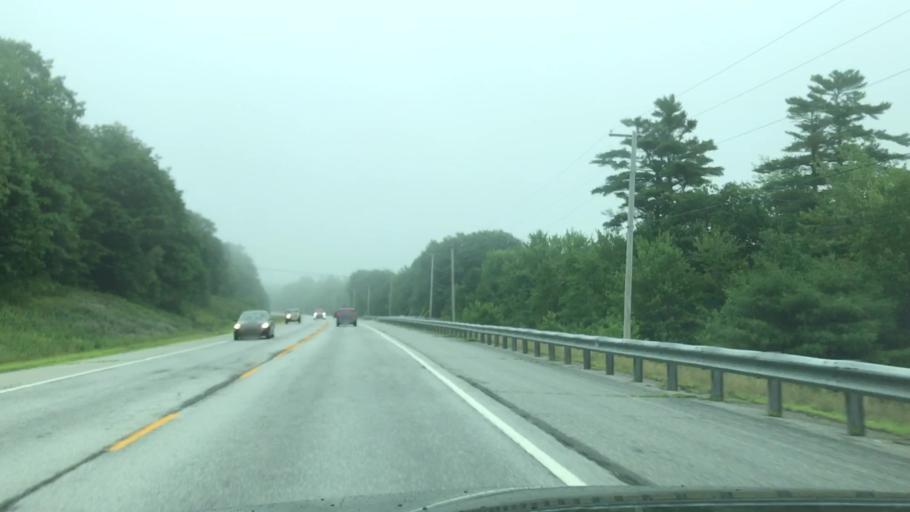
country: US
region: Maine
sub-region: Lincoln County
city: Nobleboro
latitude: 44.0753
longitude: -69.4790
